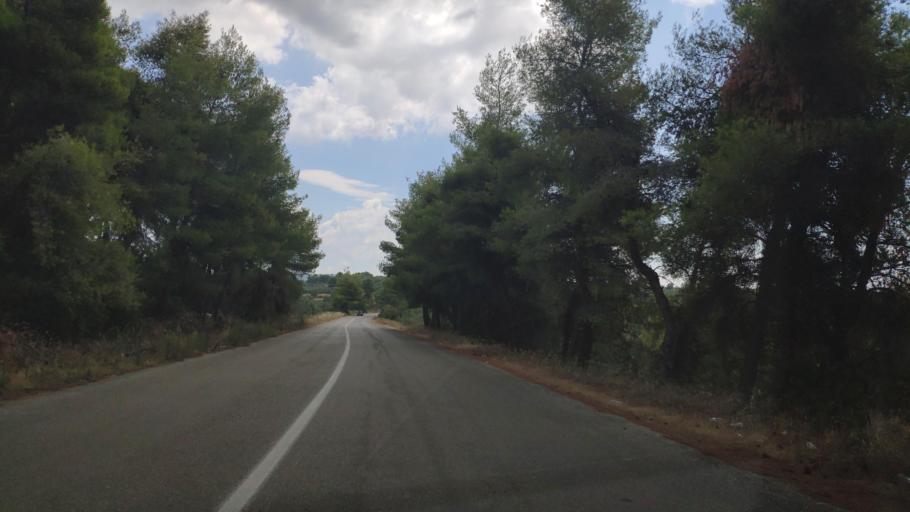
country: GR
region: Central Greece
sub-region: Nomos Fthiotidos
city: Malesina
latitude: 38.6293
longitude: 23.1760
